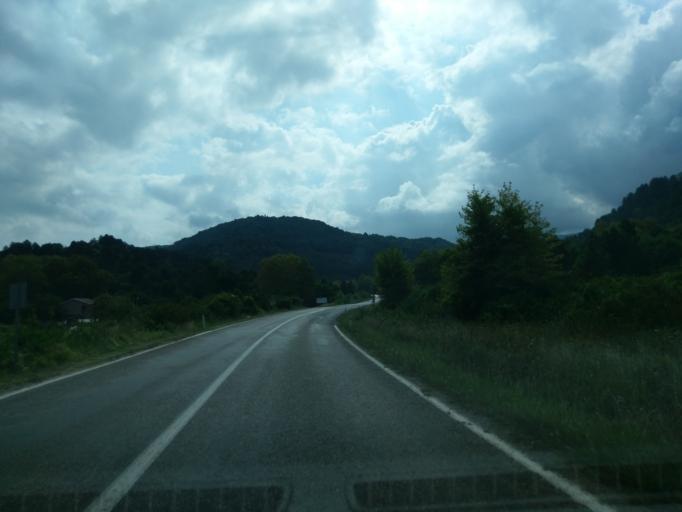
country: TR
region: Sinop
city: Yenikonak
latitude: 41.9413
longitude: 34.7179
